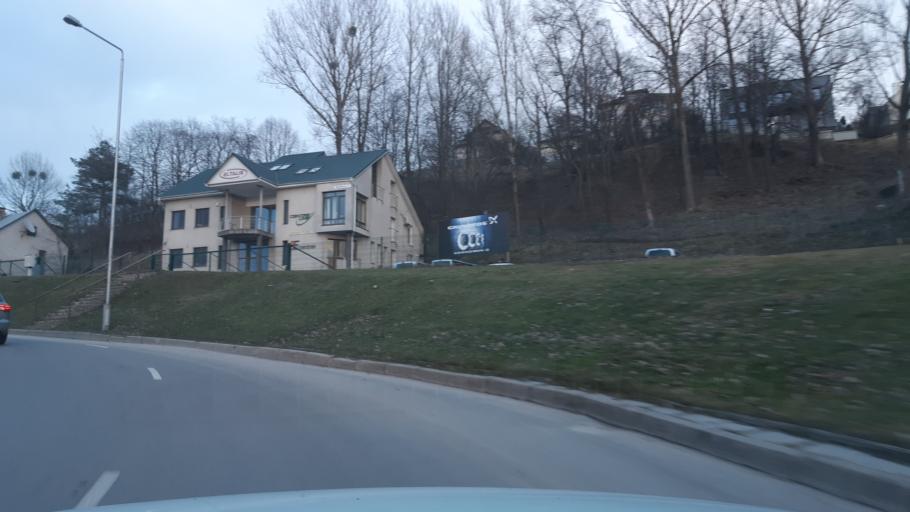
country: LT
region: Kauno apskritis
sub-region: Kaunas
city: Kaunas
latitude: 54.9126
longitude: 23.9114
